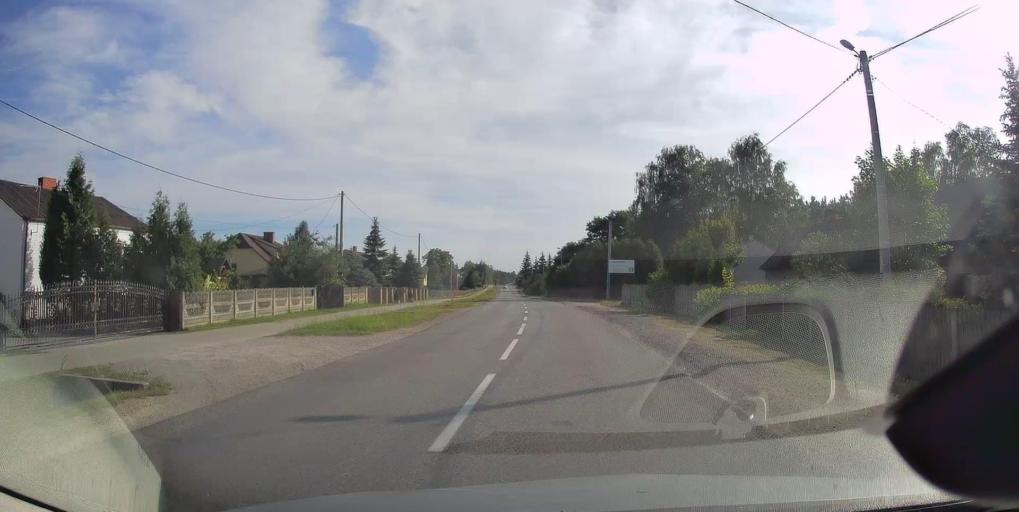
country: PL
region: Swietokrzyskie
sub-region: Powiat konecki
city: Radoszyce
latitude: 51.0860
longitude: 20.2883
